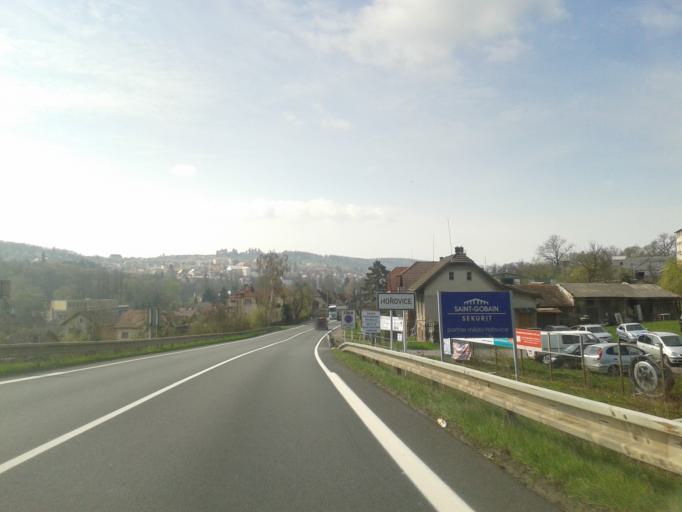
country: CZ
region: Central Bohemia
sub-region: Okres Beroun
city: Horovice
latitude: 49.8473
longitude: 13.9073
